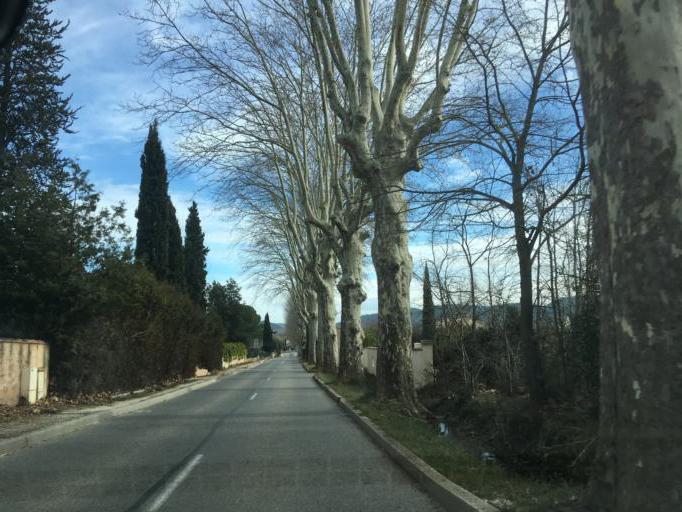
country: FR
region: Provence-Alpes-Cote d'Azur
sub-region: Departement du Var
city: Le Val
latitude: 43.4389
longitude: 6.0652
